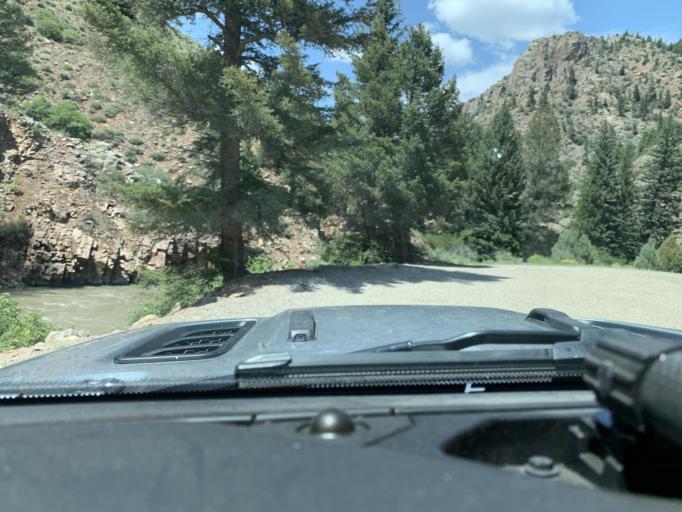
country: US
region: Colorado
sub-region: Hinsdale County
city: Lake City
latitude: 38.3490
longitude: -107.2342
